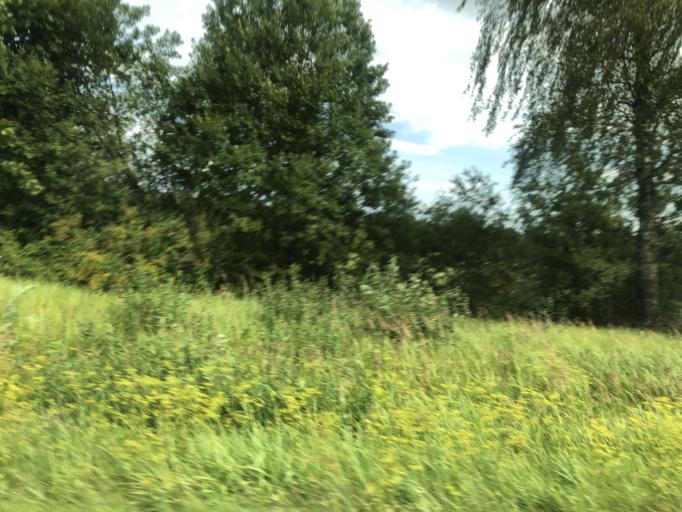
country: LV
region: Vecumnieki
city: Vecumnieki
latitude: 56.5739
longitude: 24.5342
